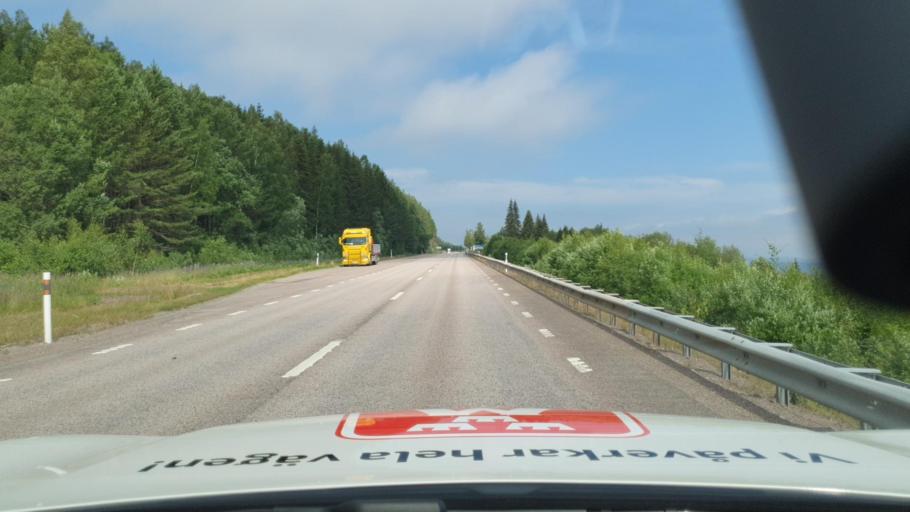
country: SE
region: Vaermland
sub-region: Sunne Kommun
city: Sunne
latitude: 59.9806
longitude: 13.1025
